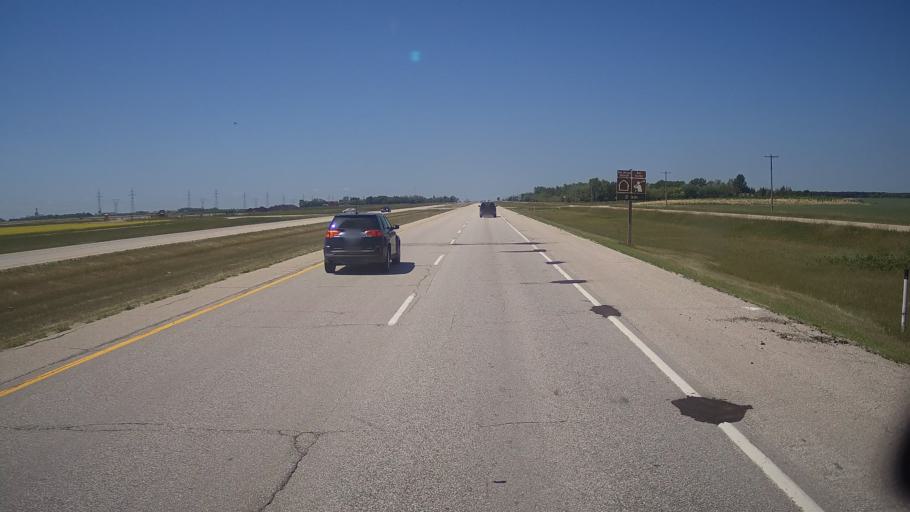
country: CA
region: Manitoba
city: Winnipeg
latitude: 49.9900
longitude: -97.2492
